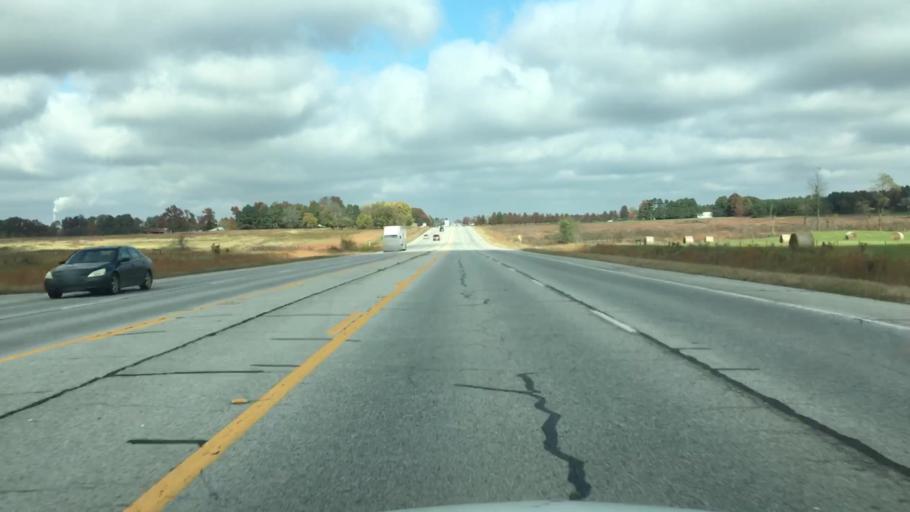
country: US
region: Arkansas
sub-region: Benton County
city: Siloam Springs
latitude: 36.2007
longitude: -94.4957
